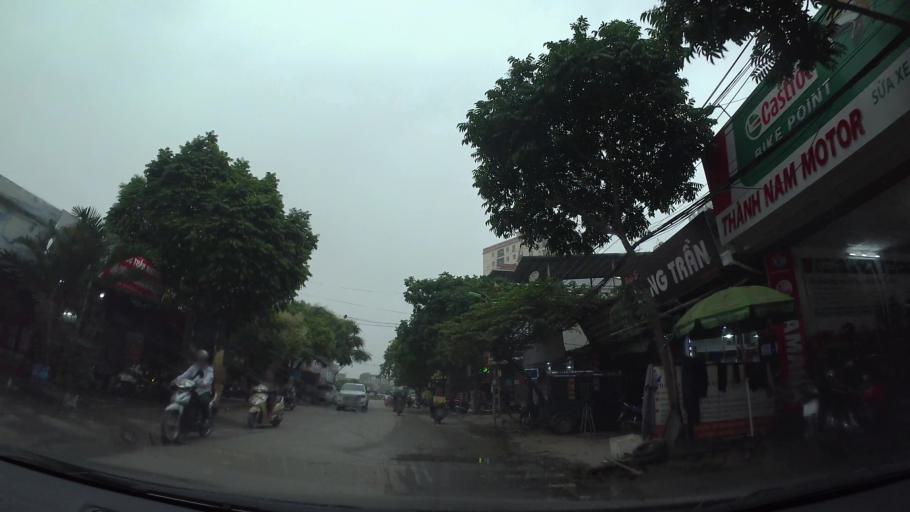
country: VN
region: Ha Noi
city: Hai BaTrung
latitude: 20.9840
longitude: 105.8343
